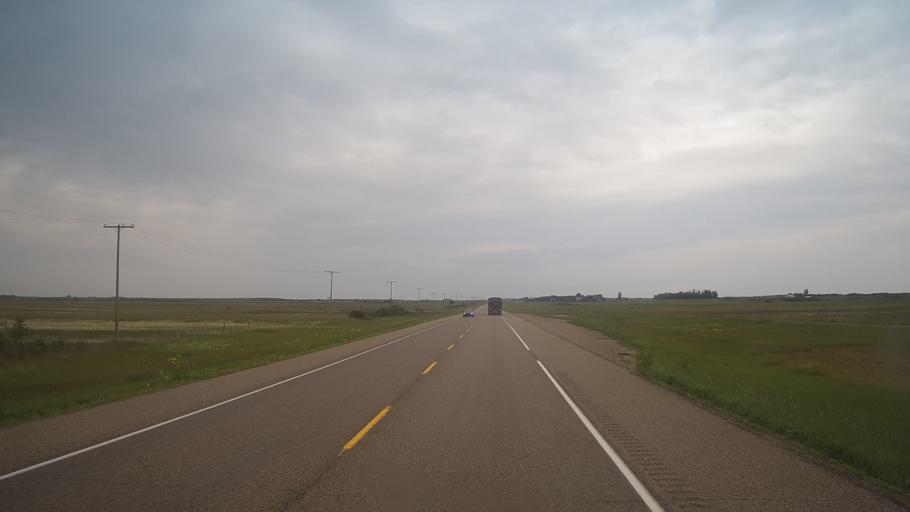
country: CA
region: Saskatchewan
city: Langham
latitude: 52.1289
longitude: -107.1472
